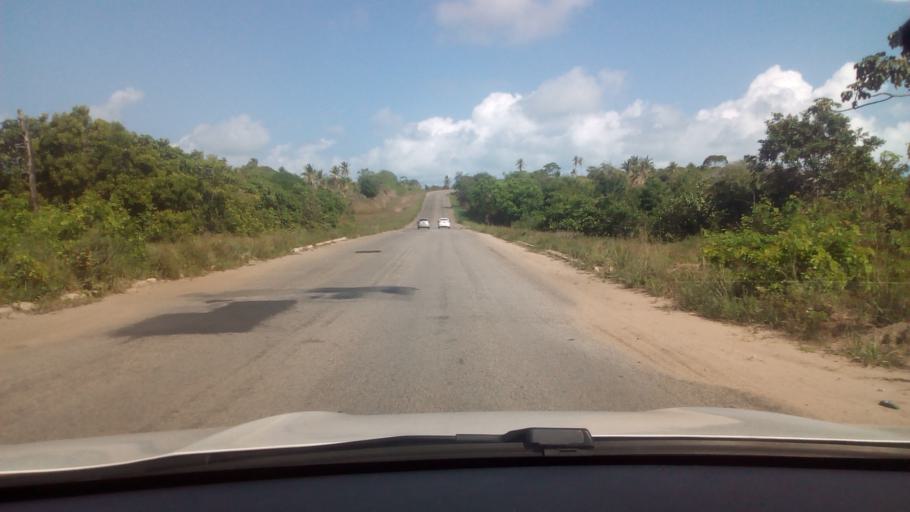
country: BR
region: Paraiba
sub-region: Conde
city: Conde
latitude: -7.2398
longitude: -34.8385
